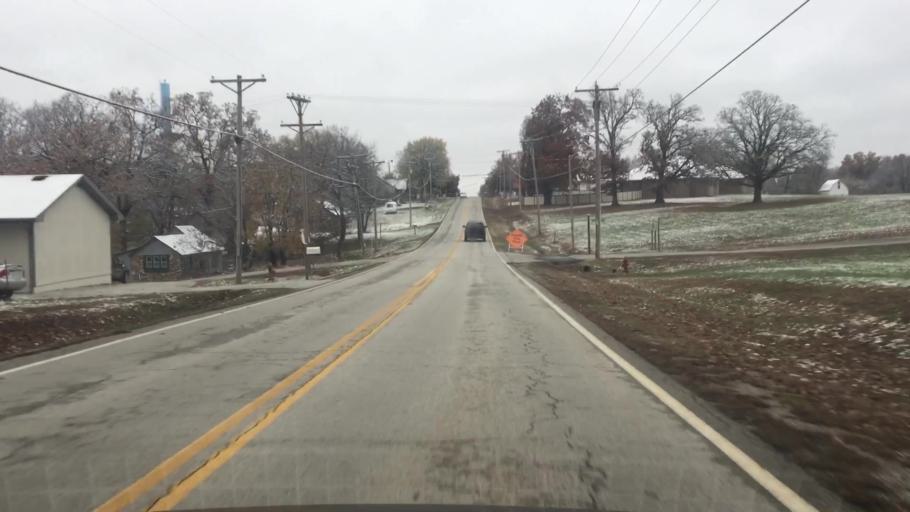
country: US
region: Missouri
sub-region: Saint Clair County
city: Osceola
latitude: 38.0325
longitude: -93.7029
